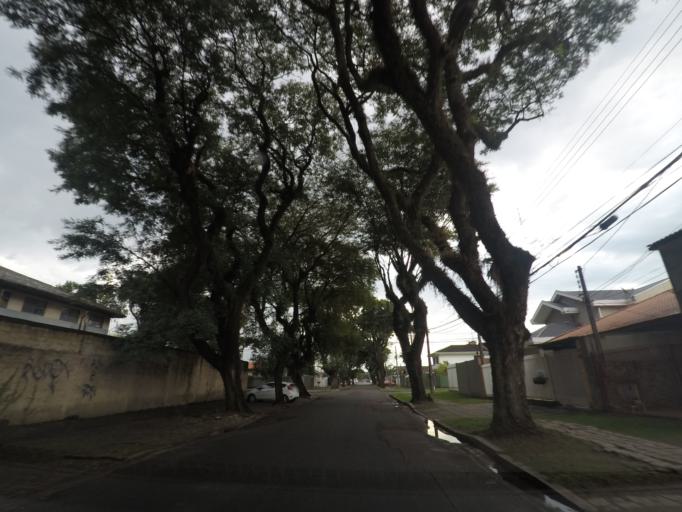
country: BR
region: Parana
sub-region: Curitiba
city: Curitiba
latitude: -25.4765
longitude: -49.2532
